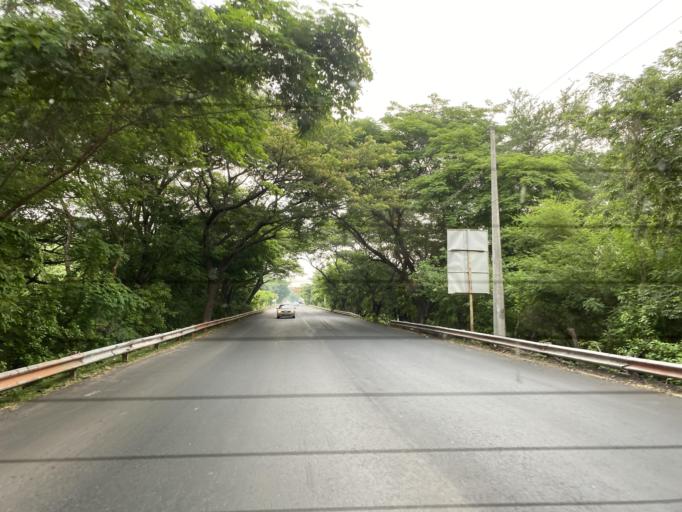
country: SV
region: San Miguel
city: Chirilagua
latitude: 13.3409
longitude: -88.1466
